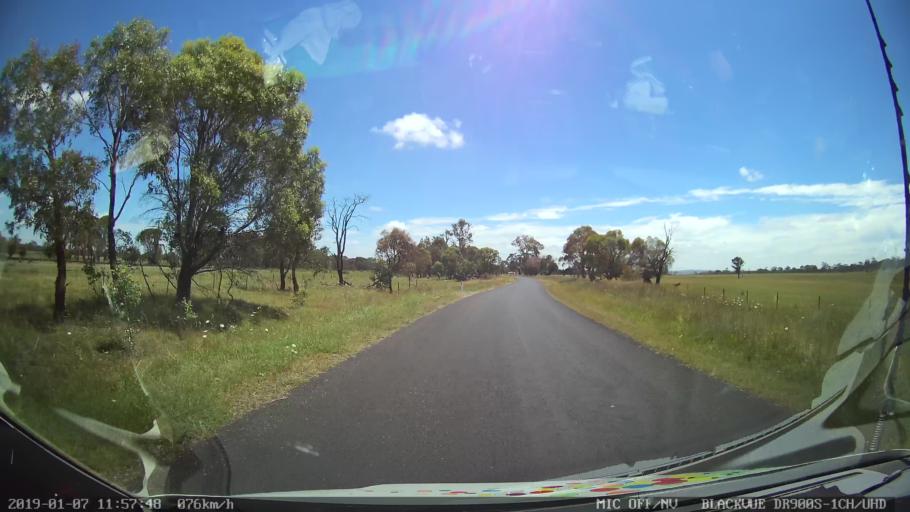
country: AU
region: New South Wales
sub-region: Guyra
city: Guyra
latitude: -30.2603
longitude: 151.6661
